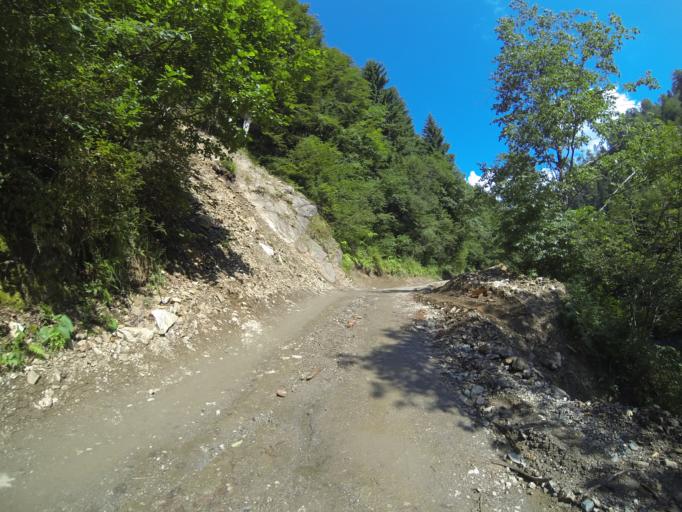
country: RO
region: Valcea
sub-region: Comuna Costesti
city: Bistrita
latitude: 45.2516
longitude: 23.9913
